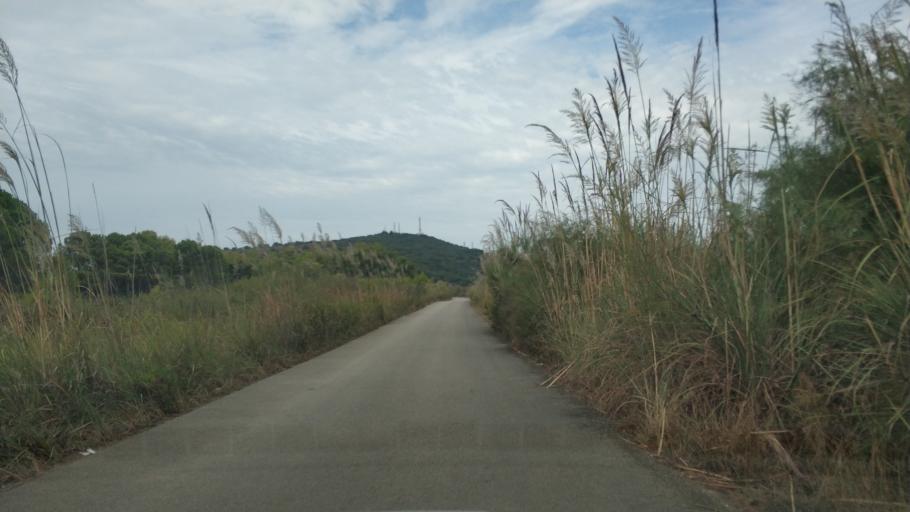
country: AL
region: Vlore
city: Vlore
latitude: 40.5030
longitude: 19.4265
